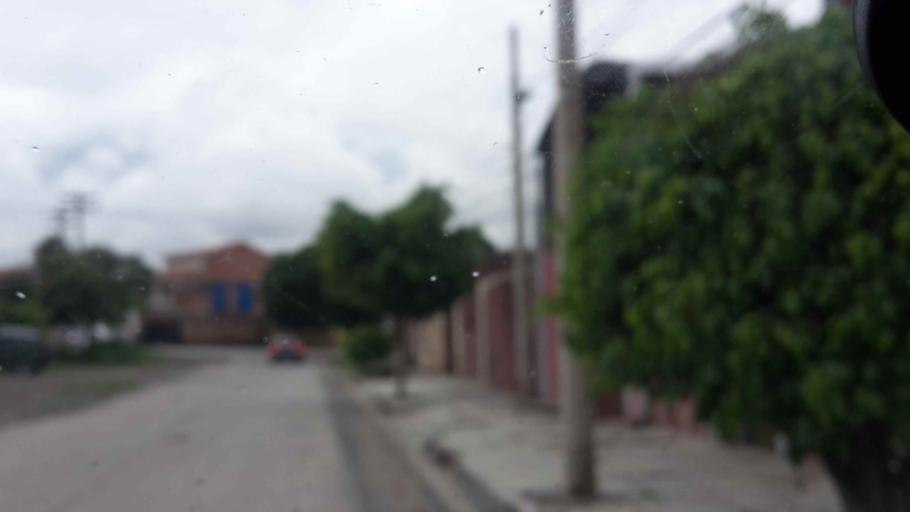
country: BO
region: Cochabamba
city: Cochabamba
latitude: -17.3757
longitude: -66.1237
